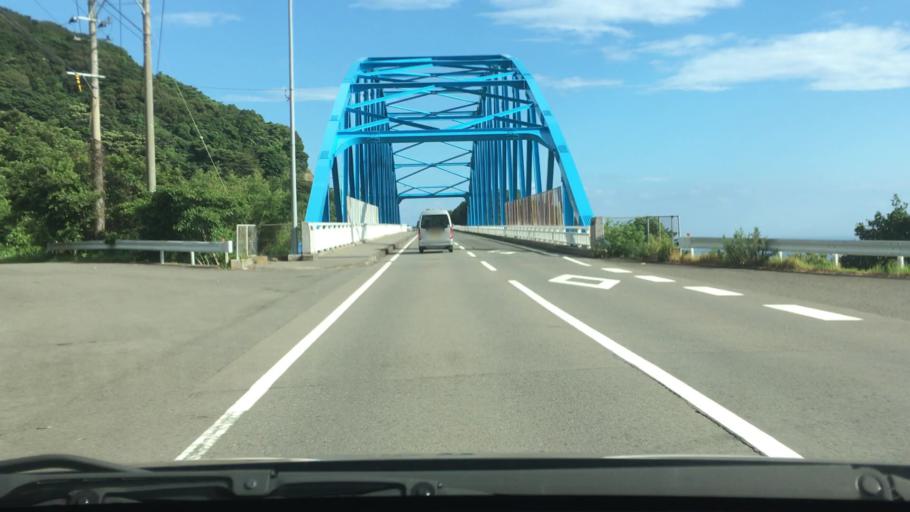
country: JP
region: Nagasaki
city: Togitsu
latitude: 32.8517
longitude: 129.6900
